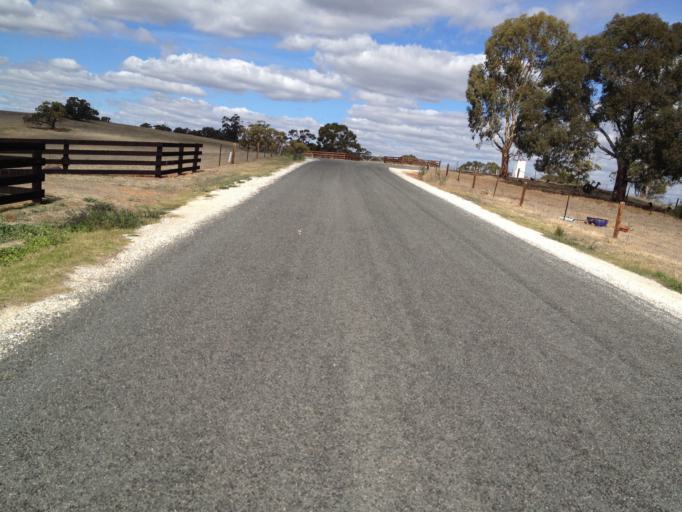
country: AU
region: South Australia
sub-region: Barossa
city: Lyndoch
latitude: -34.6307
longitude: 138.8310
